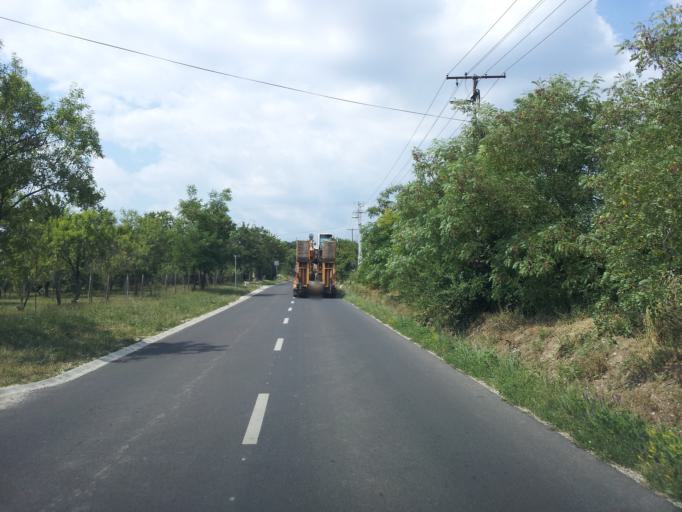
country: HU
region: Veszprem
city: Zanka
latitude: 46.8857
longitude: 17.7444
